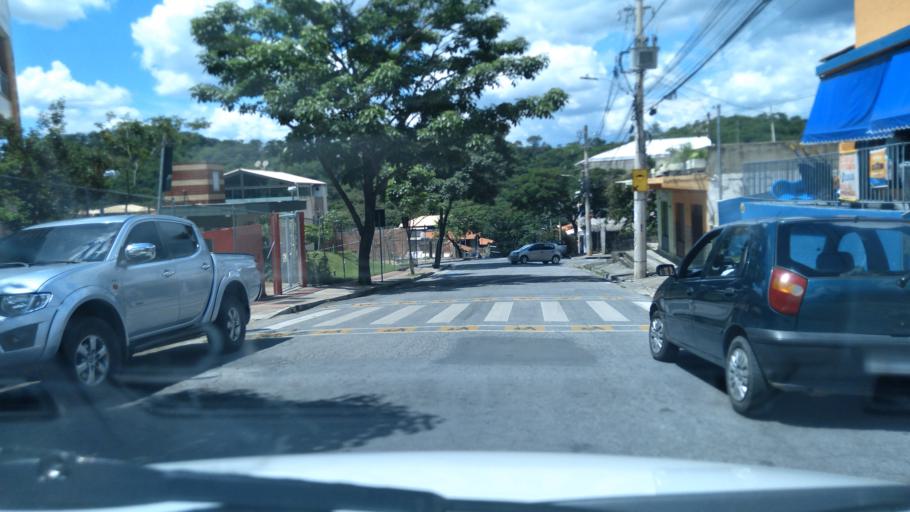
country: BR
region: Minas Gerais
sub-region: Santa Luzia
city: Santa Luzia
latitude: -19.8577
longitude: -43.8720
